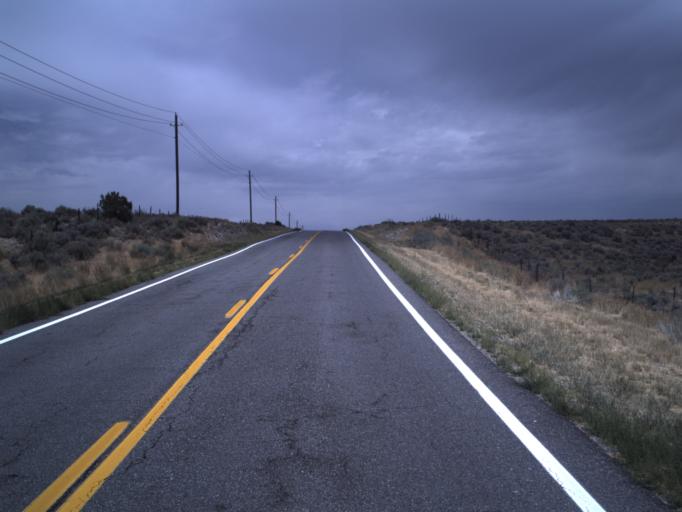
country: US
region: Utah
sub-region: Tooele County
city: Tooele
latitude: 40.3459
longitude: -112.3066
